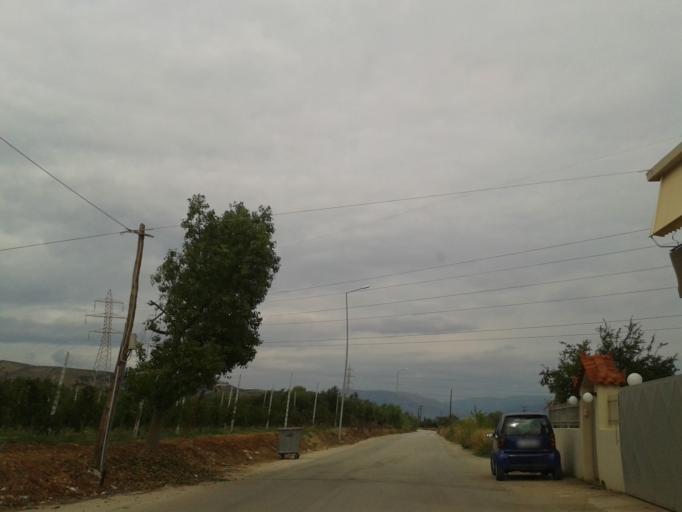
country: GR
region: Peloponnese
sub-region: Nomos Argolidos
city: Argos
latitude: 37.6055
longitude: 22.6976
